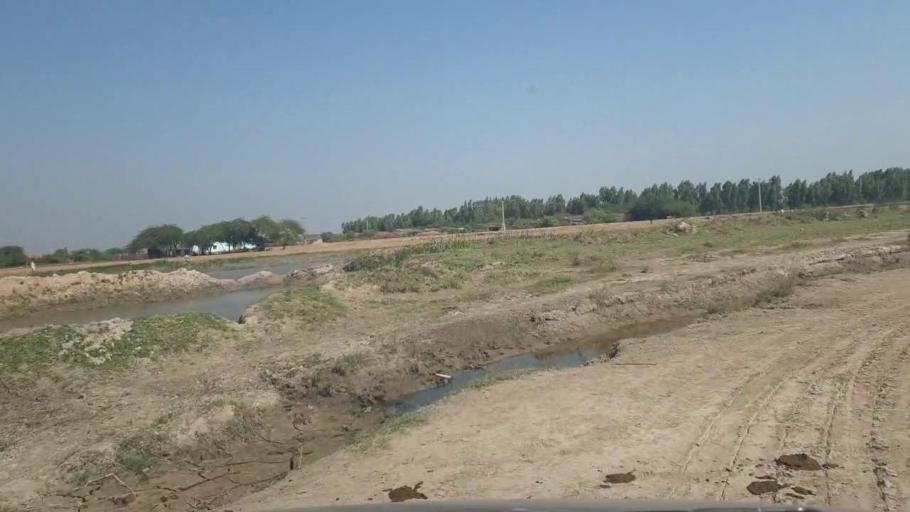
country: PK
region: Sindh
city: Badin
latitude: 24.6796
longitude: 68.8990
